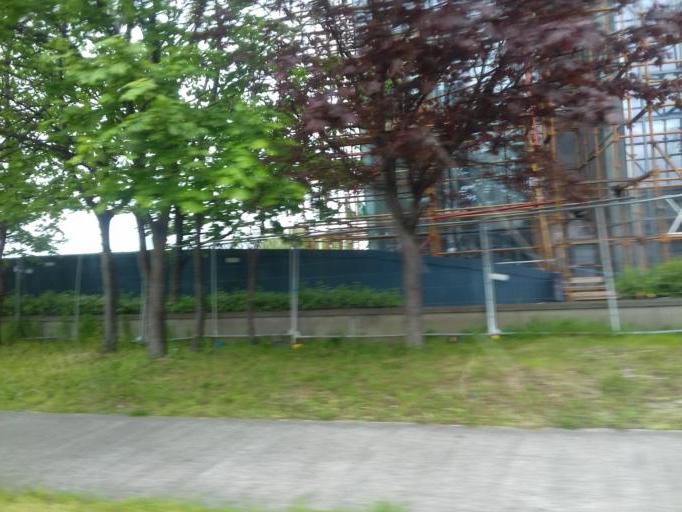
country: IE
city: Cherry Orchard
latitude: 53.3182
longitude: -6.3649
